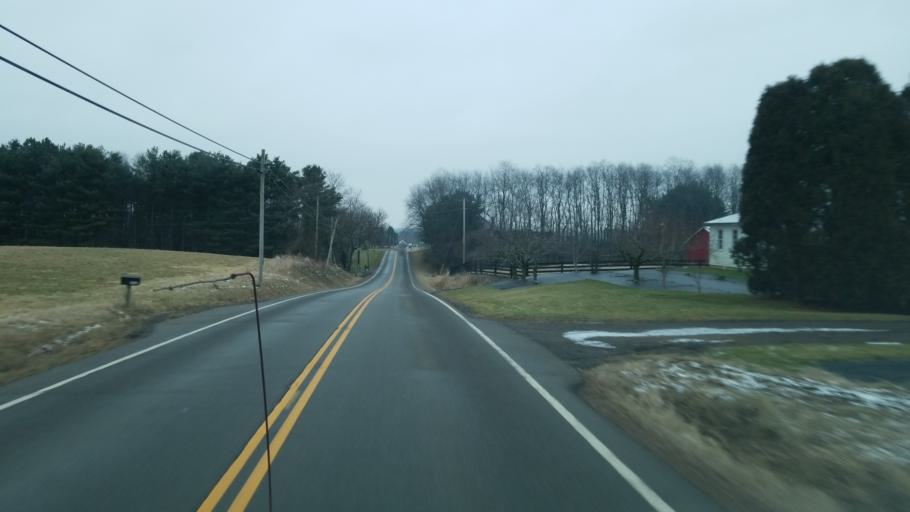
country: US
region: Ohio
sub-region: Wayne County
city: Shreve
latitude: 40.7681
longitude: -82.0154
